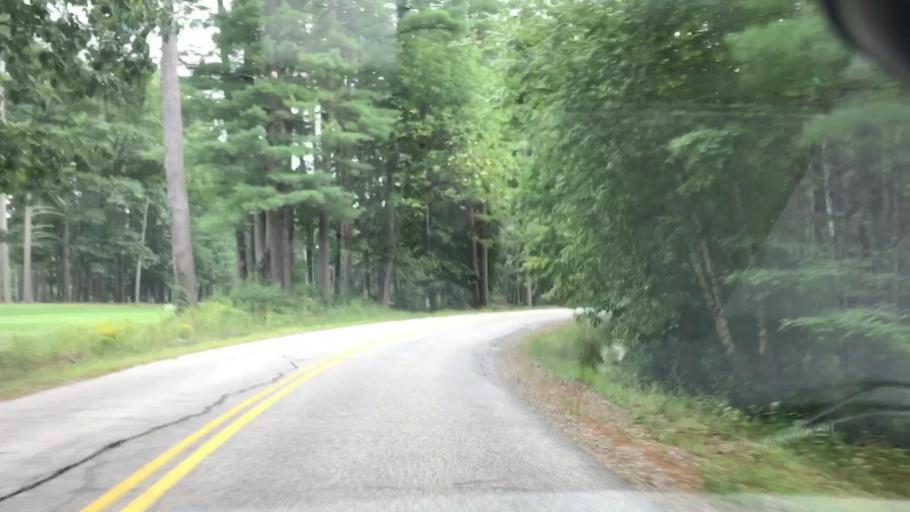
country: US
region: New Hampshire
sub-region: Hillsborough County
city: Merrimack
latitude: 42.8503
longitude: -71.5705
